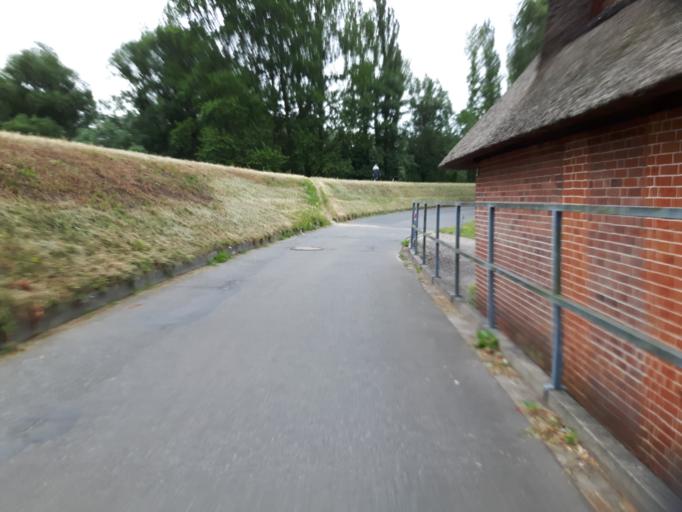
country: DE
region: Lower Saxony
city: Winsen
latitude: 53.3789
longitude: 10.2019
